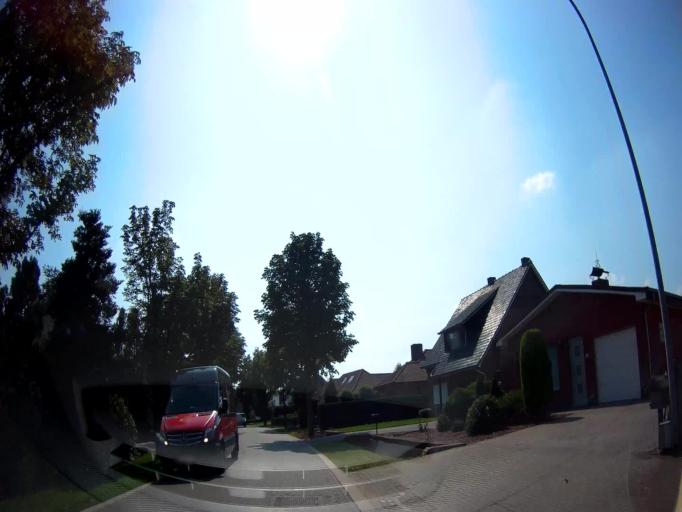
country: BE
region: Flanders
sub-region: Provincie Antwerpen
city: Oud-Turnhout
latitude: 51.3030
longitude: 4.9880
